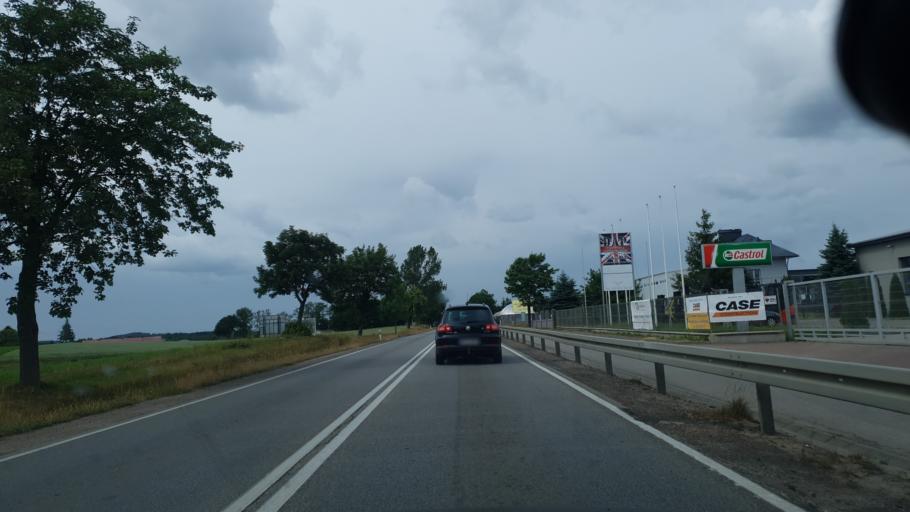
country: PL
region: Pomeranian Voivodeship
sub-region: Powiat kartuski
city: Zukowo
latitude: 54.3831
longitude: 18.3613
